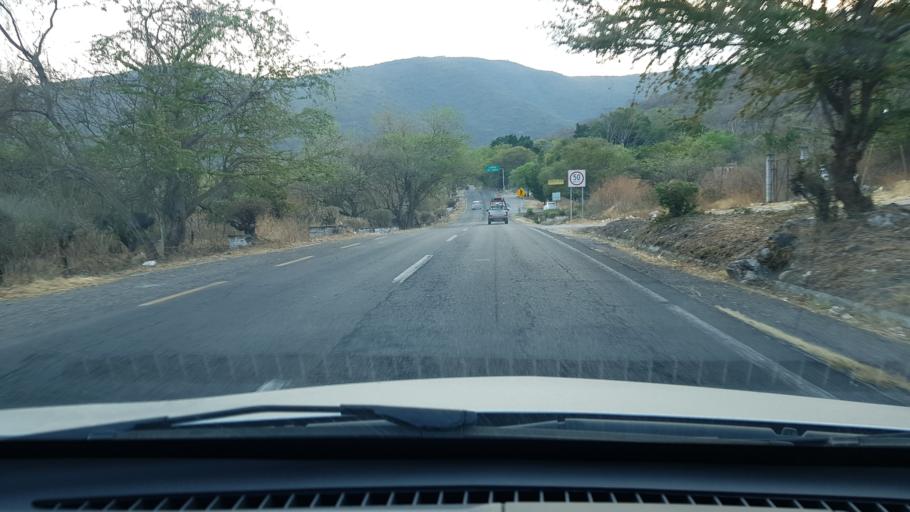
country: MX
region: Morelos
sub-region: Jiutepec
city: Independencia
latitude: 18.8585
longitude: -99.1060
